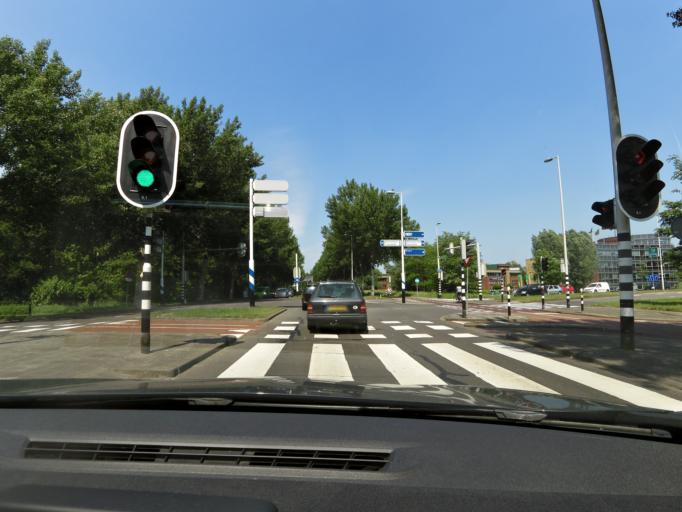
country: NL
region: South Holland
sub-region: Gemeente Rotterdam
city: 's-Gravenland
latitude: 51.9254
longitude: 4.5335
